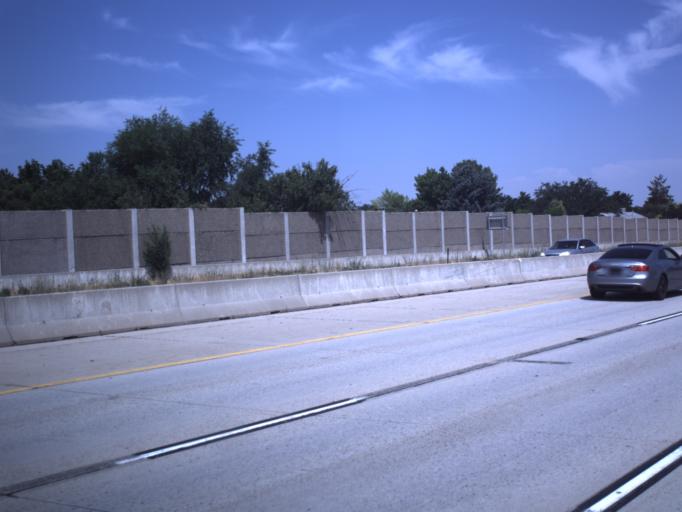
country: US
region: Utah
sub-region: Salt Lake County
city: Kearns
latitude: 40.6744
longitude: -111.9814
